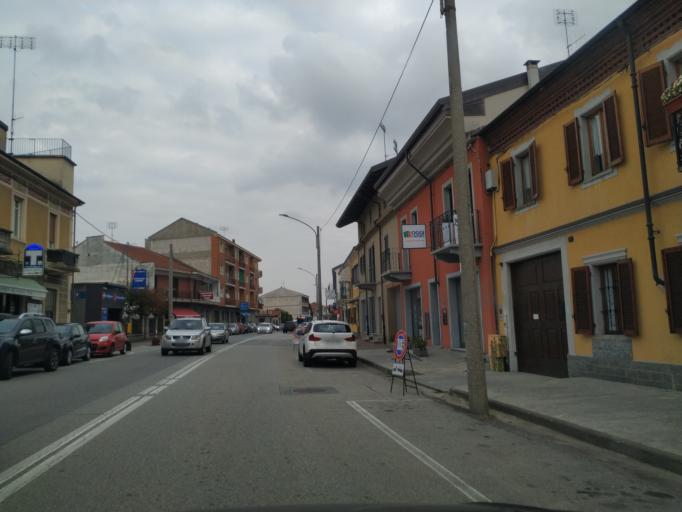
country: IT
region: Piedmont
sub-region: Provincia di Torino
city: Chivasso
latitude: 45.1917
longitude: 7.8968
